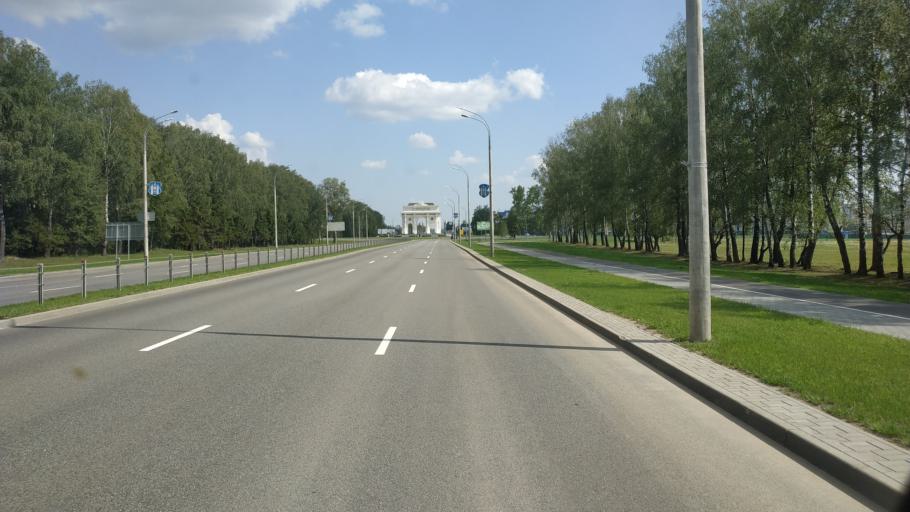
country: BY
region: Mogilev
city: Buynichy
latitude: 53.9383
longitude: 30.2459
